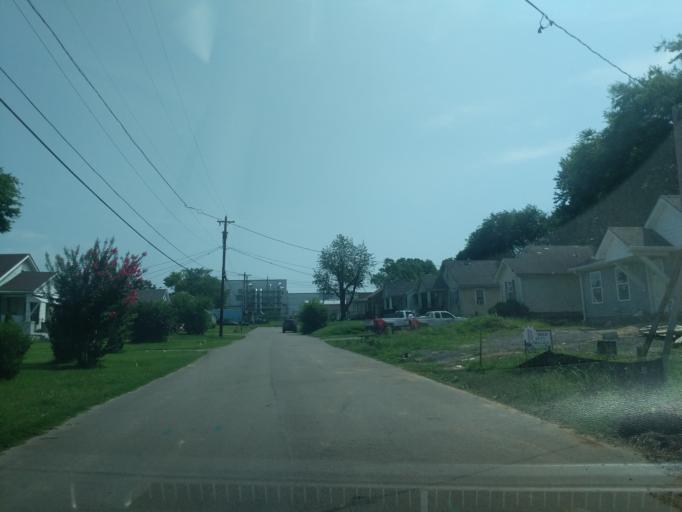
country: US
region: Tennessee
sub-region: Davidson County
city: Lakewood
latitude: 36.2719
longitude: -86.6666
